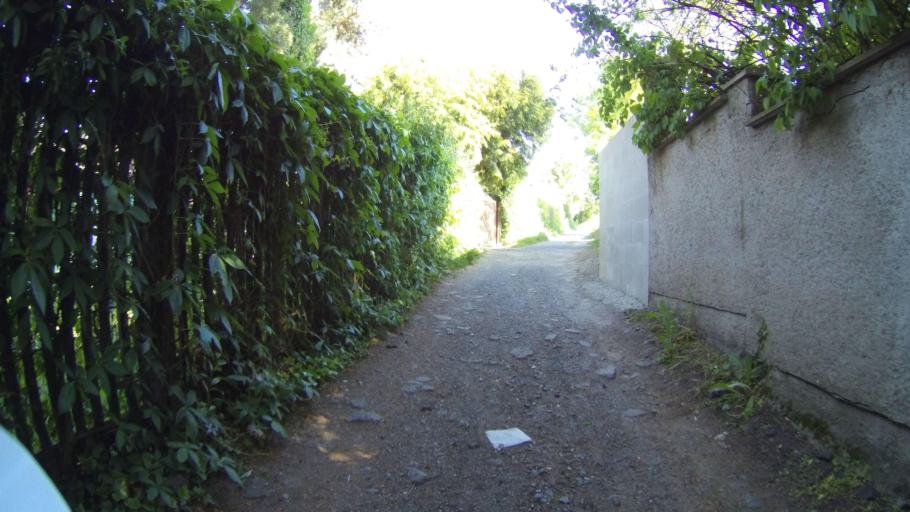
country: CZ
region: Central Bohemia
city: Klecany
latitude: 50.1679
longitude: 14.4292
